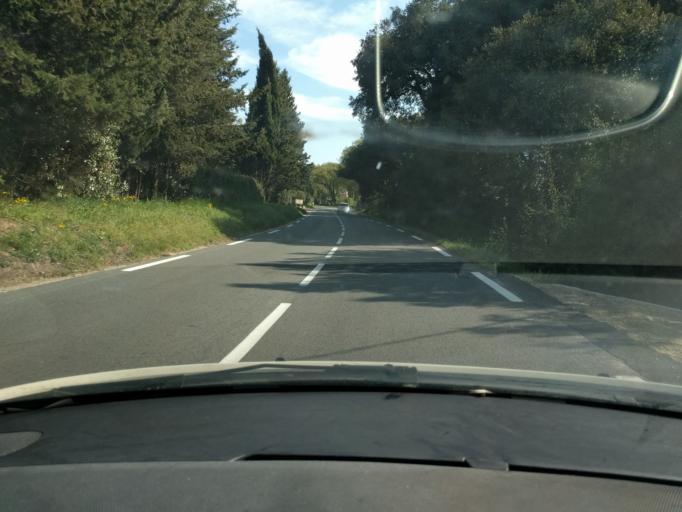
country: FR
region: Provence-Alpes-Cote d'Azur
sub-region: Departement du Var
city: La Crau
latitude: 43.1681
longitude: 6.1186
